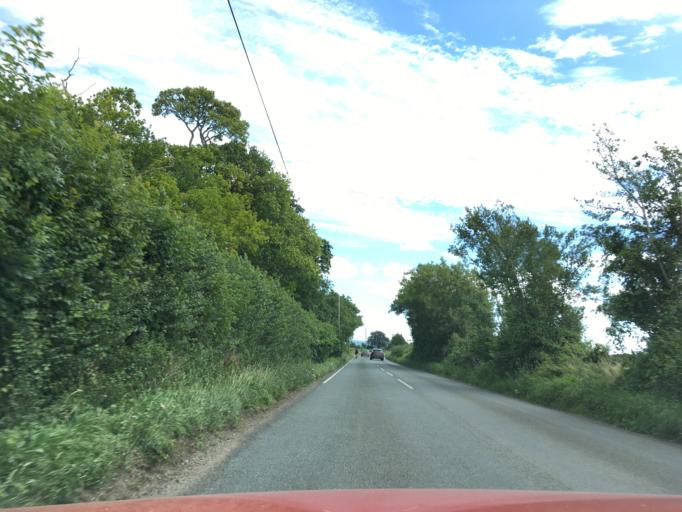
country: GB
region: England
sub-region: Somerset
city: Ilchester
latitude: 51.0751
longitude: -2.6860
